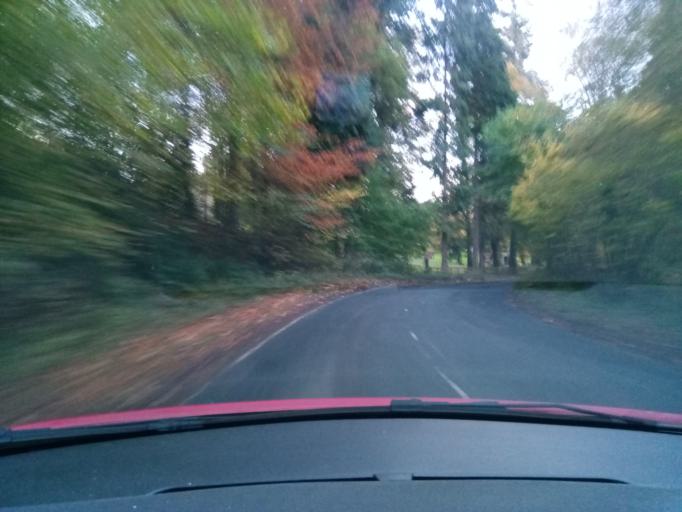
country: GB
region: England
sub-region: Northumberland
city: Bardon Mill
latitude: 54.9551
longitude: -2.2567
